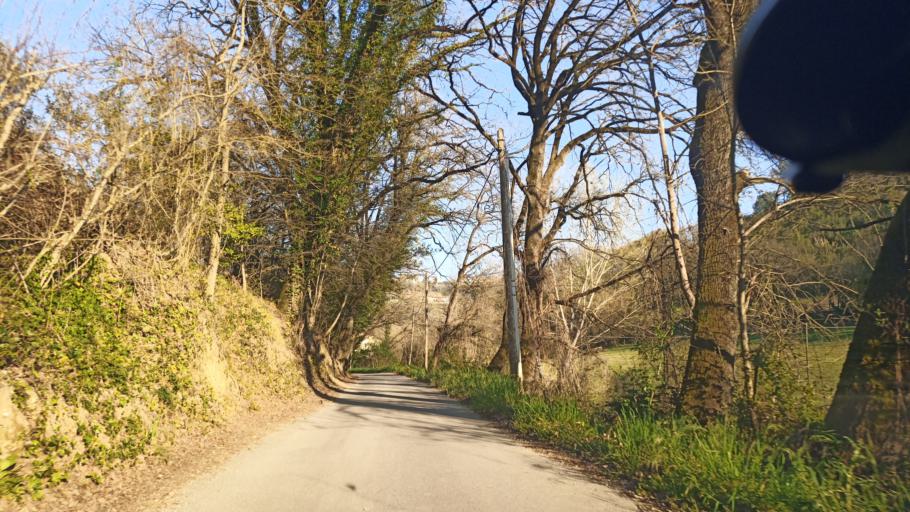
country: IT
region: Latium
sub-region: Provincia di Rieti
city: Poggio Mirteto
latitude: 42.2623
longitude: 12.6725
